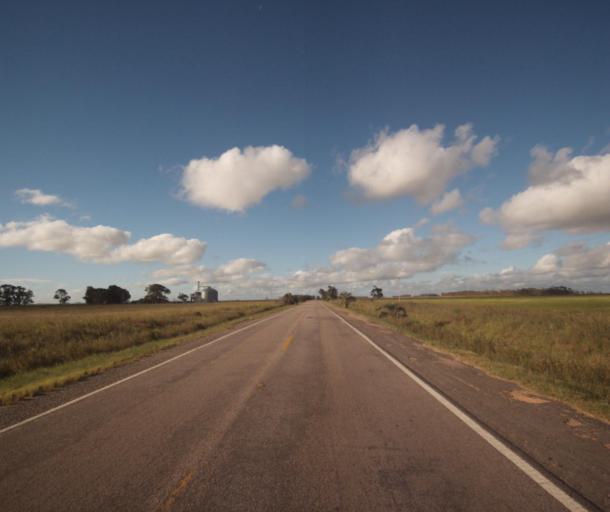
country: BR
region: Rio Grande do Sul
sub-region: Arroio Grande
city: Arroio Grande
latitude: -32.4478
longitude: -52.5698
